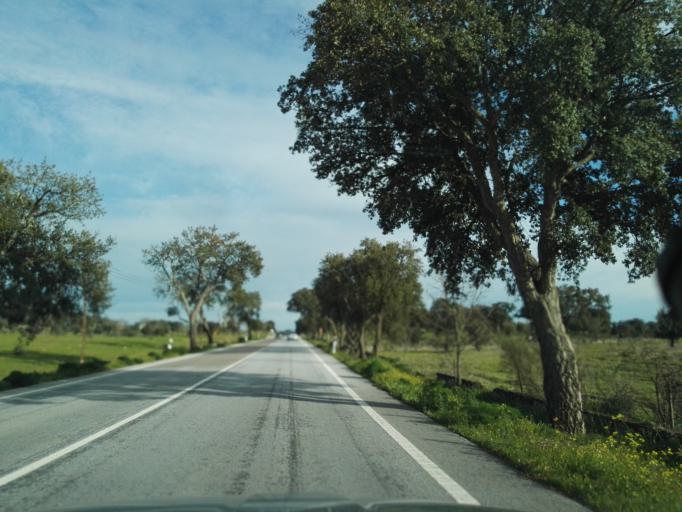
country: PT
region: Portalegre
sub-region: Portalegre
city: Alagoa
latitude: 39.3669
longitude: -7.5578
